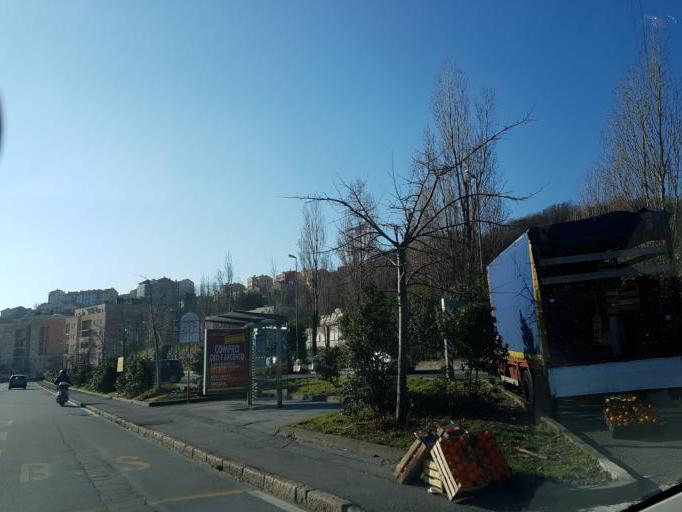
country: IT
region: Liguria
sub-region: Provincia di Genova
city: Santa Marta
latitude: 44.4767
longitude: 8.8993
